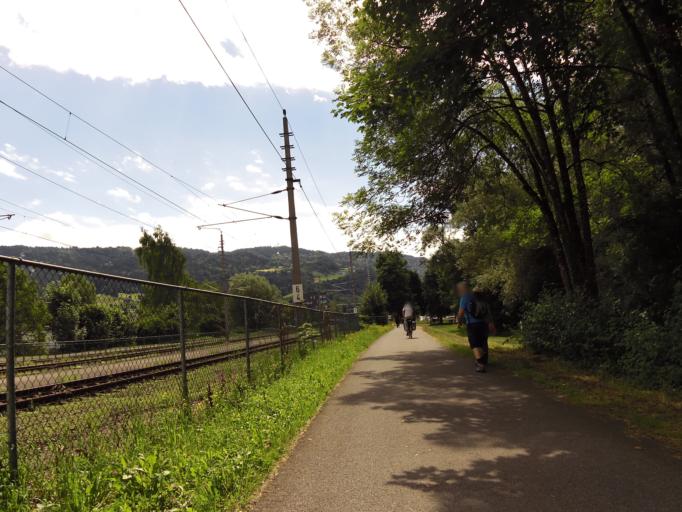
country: AT
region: Vorarlberg
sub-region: Politischer Bezirk Bregenz
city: Lochau
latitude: 47.5313
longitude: 9.7400
